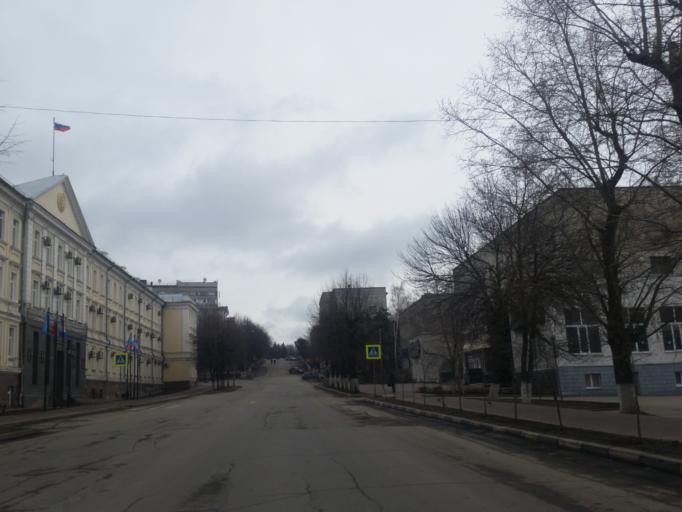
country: RU
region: Ulyanovsk
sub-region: Ulyanovskiy Rayon
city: Ulyanovsk
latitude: 54.3115
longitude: 48.4001
